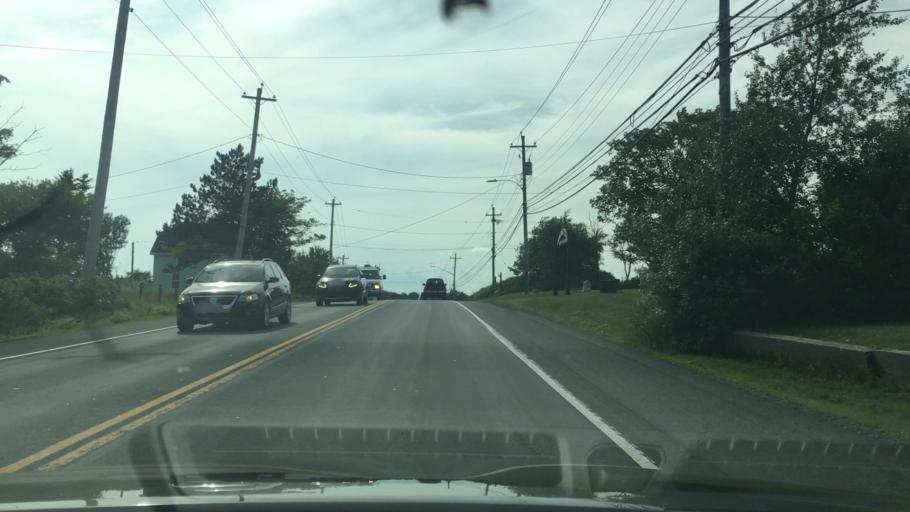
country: CA
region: Nova Scotia
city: Dartmouth
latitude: 44.7336
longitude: -63.7650
